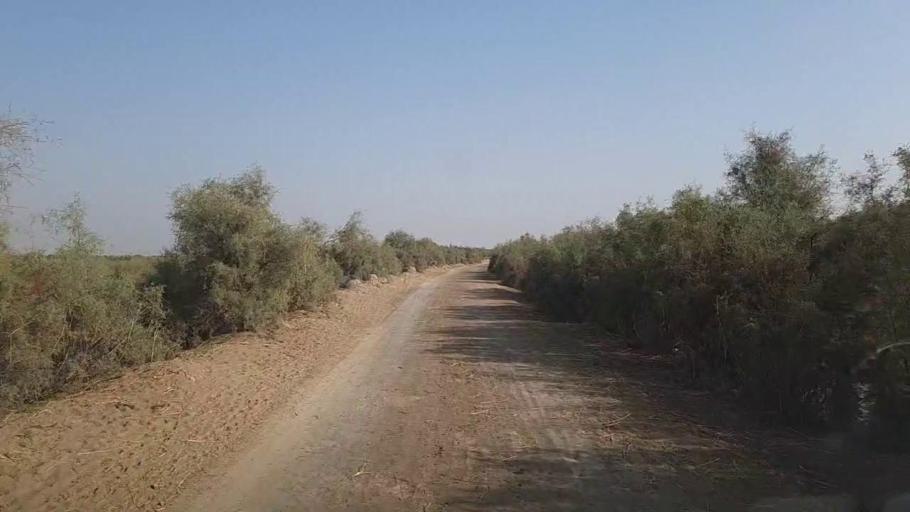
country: PK
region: Sindh
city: Kandhkot
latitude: 28.3578
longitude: 69.3325
